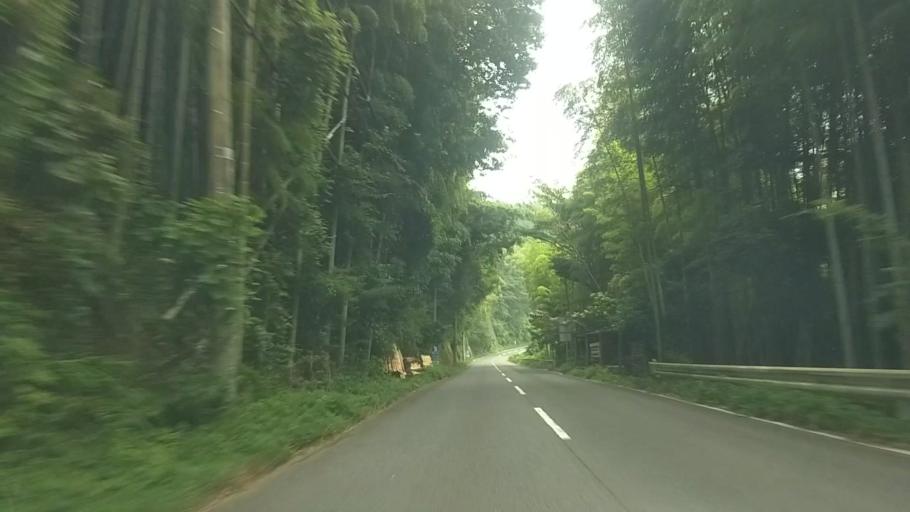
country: JP
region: Chiba
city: Katsuura
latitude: 35.2440
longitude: 140.2422
